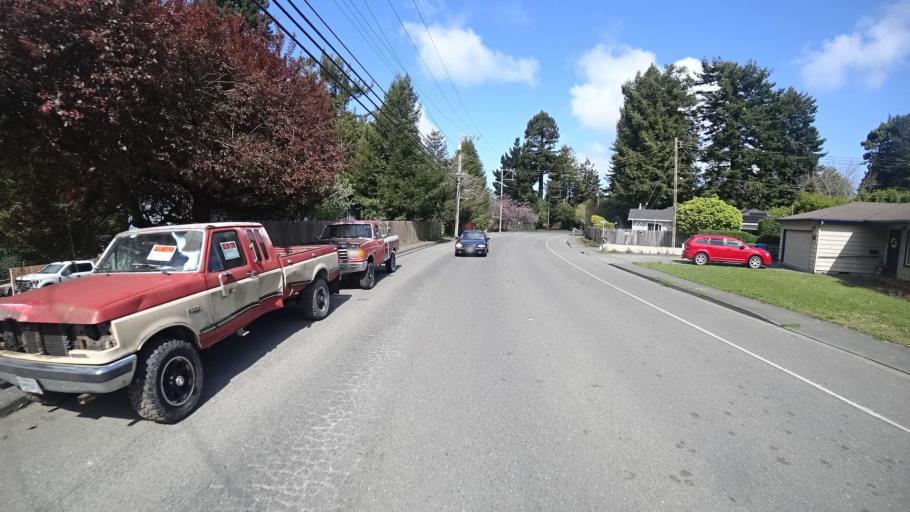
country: US
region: California
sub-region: Humboldt County
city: Cutten
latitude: 40.7590
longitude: -124.1534
